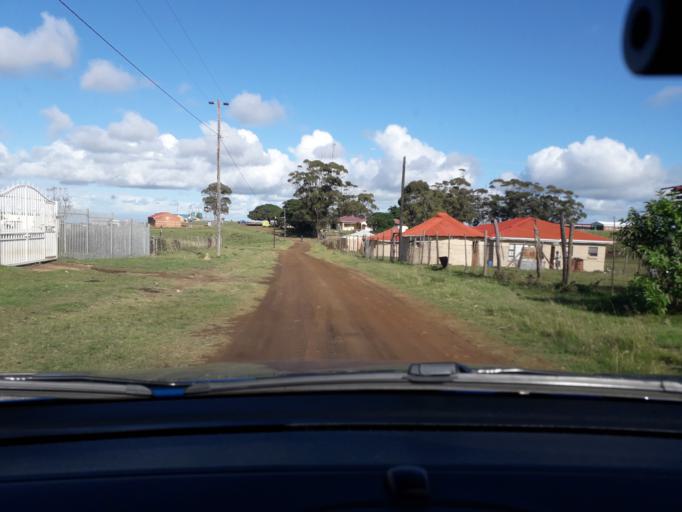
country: ZA
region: Eastern Cape
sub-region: Buffalo City Metropolitan Municipality
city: Bhisho
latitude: -33.1099
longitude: 27.4244
